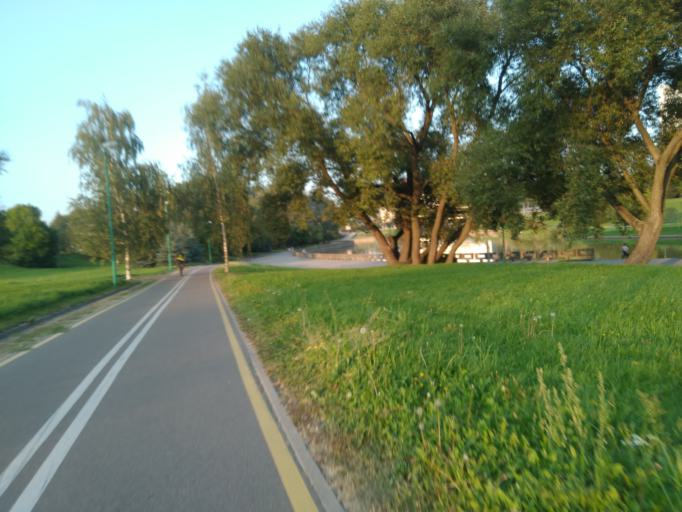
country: BY
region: Minsk
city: Minsk
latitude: 53.9156
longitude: 27.5436
